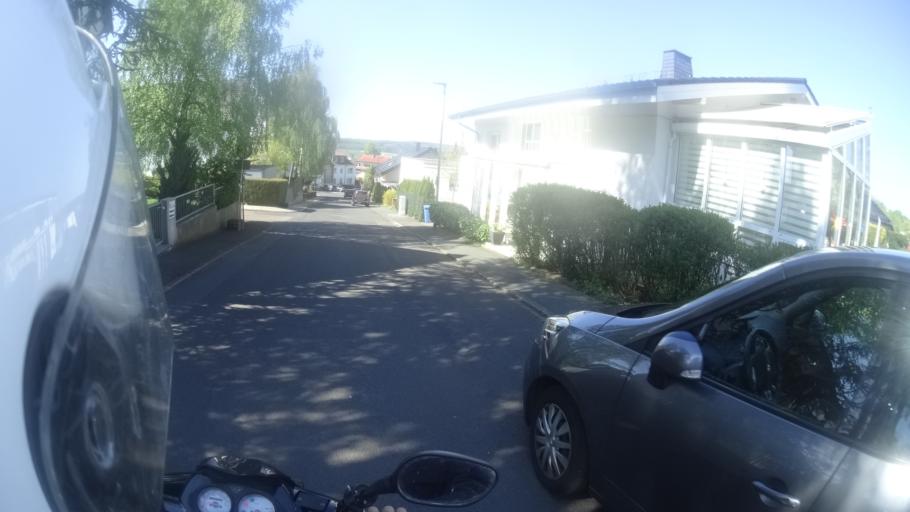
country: DE
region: Hesse
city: Taunusstein
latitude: 50.1308
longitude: 8.1467
